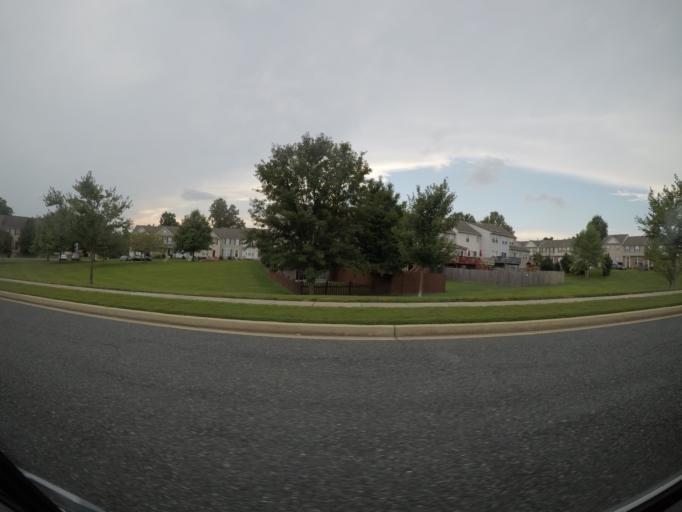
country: US
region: Maryland
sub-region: Harford County
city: Joppatowne
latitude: 39.4717
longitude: -76.3296
